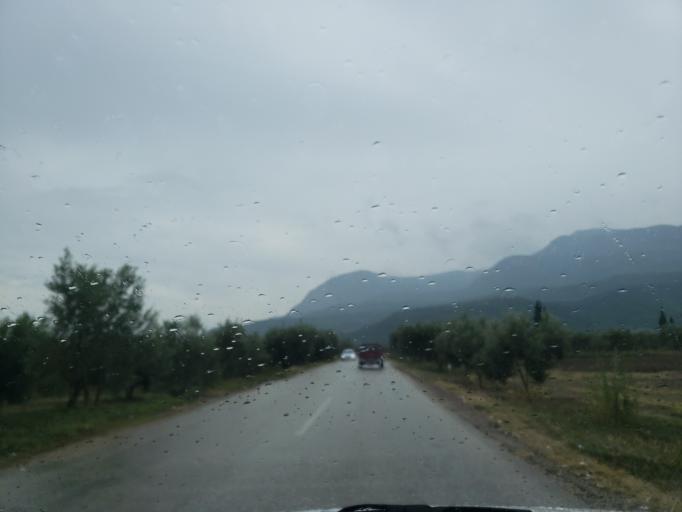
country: GR
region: Central Greece
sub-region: Nomos Fthiotidos
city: Anthili
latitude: 38.8035
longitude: 22.4555
